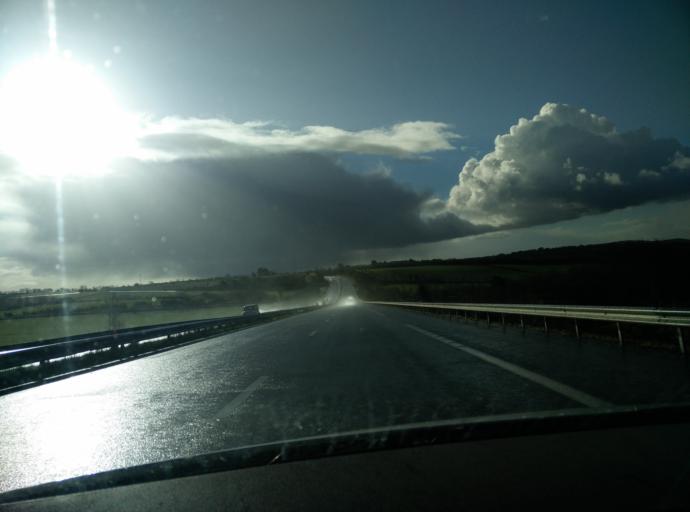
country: FR
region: Brittany
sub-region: Departement du Finistere
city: Hopital-Camfrout
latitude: 48.3262
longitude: -4.2255
